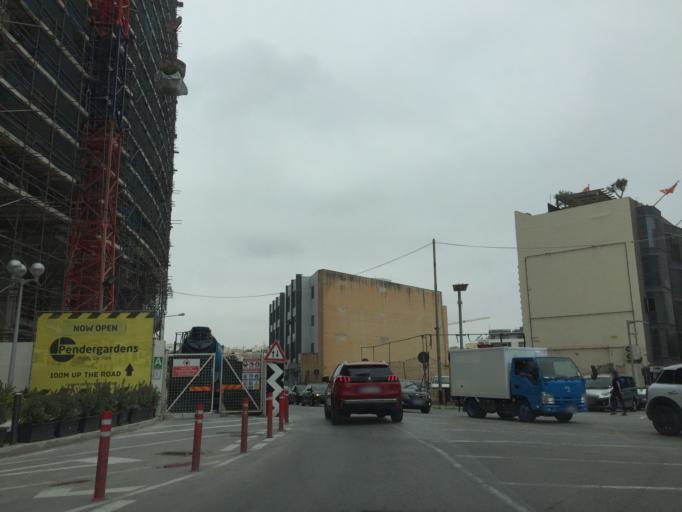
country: MT
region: Saint Julian
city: San Giljan
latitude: 35.9223
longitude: 14.4888
